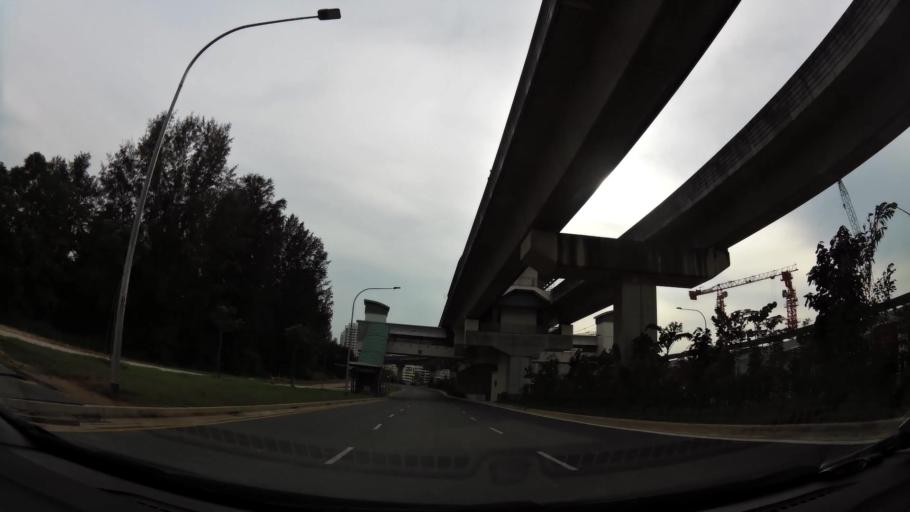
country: MY
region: Johor
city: Kampung Pasir Gudang Baru
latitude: 1.4162
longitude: 103.9025
